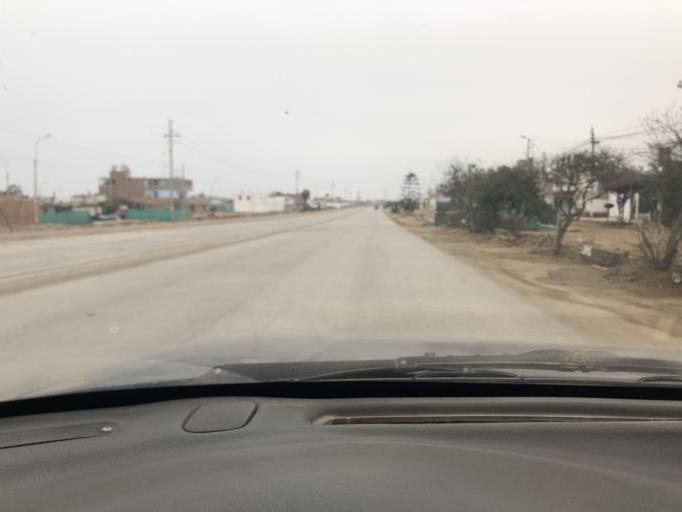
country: PE
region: Lima
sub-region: Lima
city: San Bartolo
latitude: -12.3718
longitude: -76.7878
